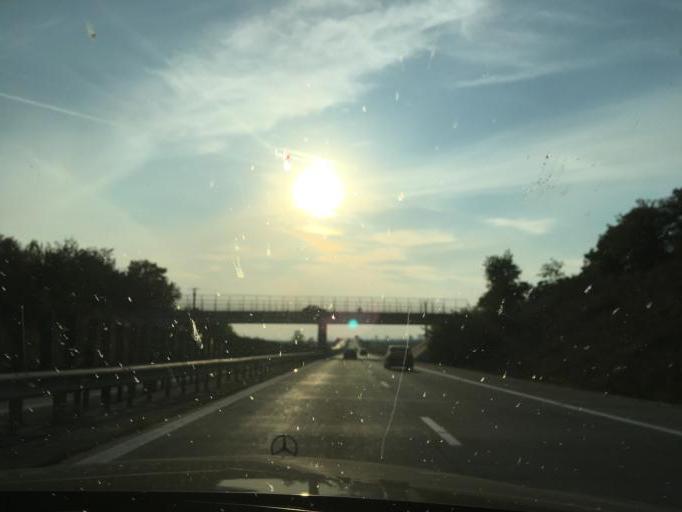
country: RO
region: Ilfov
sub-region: Comuna Cernica
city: Cernica
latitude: 44.4136
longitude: 26.2987
